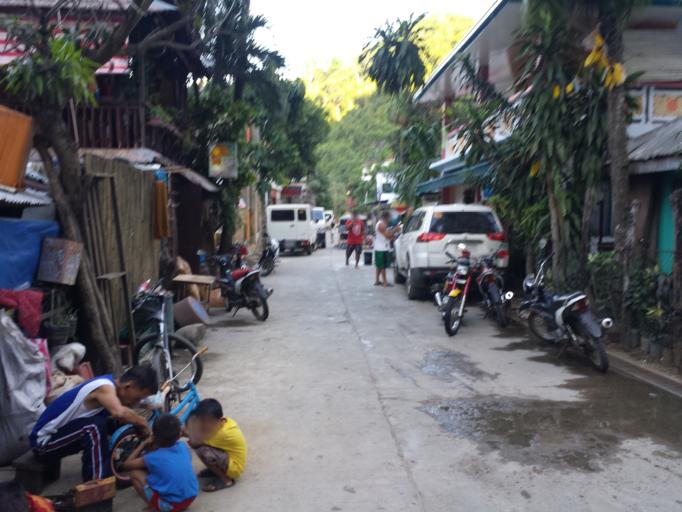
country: PH
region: Mimaropa
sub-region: Province of Palawan
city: El Nido
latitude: 11.1782
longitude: 119.3901
